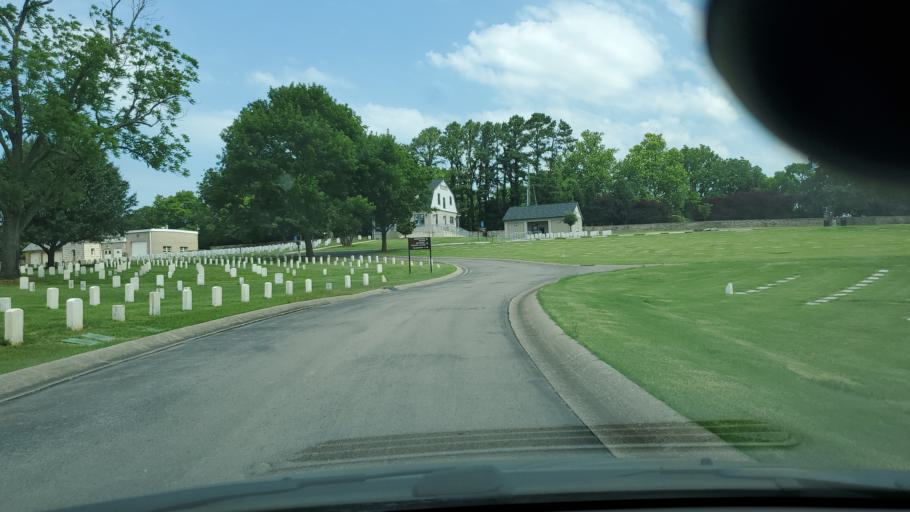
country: US
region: Tennessee
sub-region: Davidson County
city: Goodlettsville
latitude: 36.2422
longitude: -86.7266
